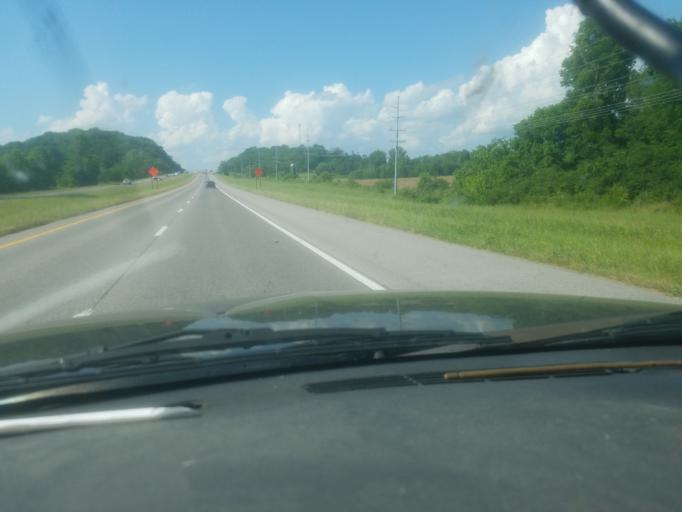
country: US
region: Tennessee
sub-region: Maury County
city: Mount Pleasant
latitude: 35.5280
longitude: -87.2220
